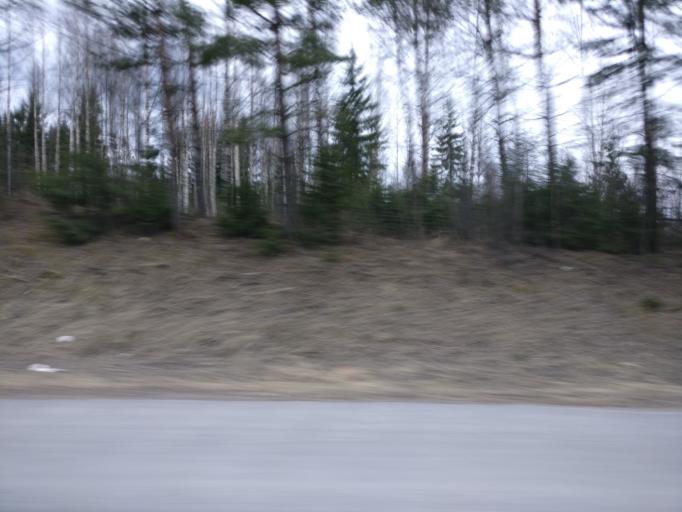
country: FI
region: Haeme
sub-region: Riihimaeki
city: Riihimaeki
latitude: 60.6776
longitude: 24.7646
